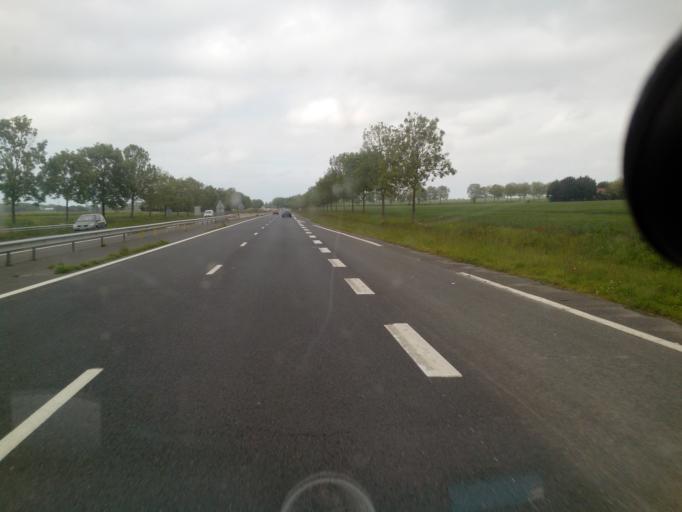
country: FR
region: Lower Normandy
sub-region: Departement du Calvados
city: Mathieu
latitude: 49.2608
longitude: -0.3820
